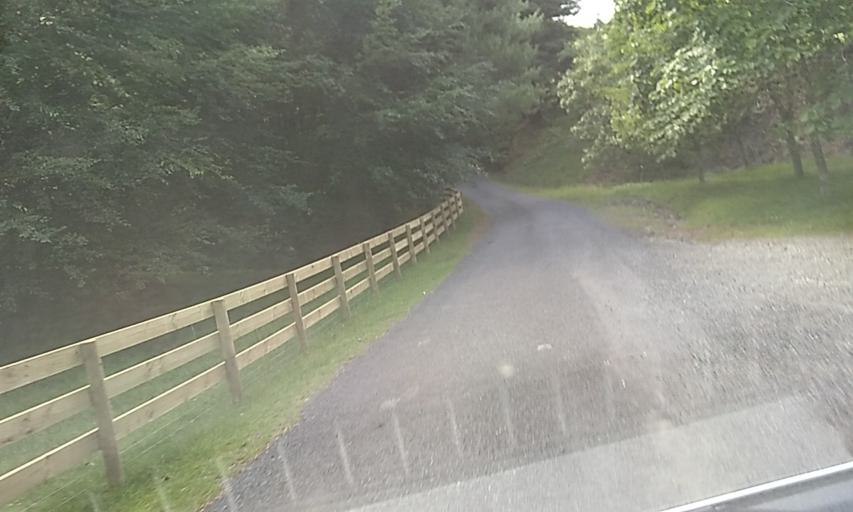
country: NZ
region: Bay of Plenty
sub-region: Tauranga City
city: Tauranga
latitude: -37.8159
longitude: 176.0434
